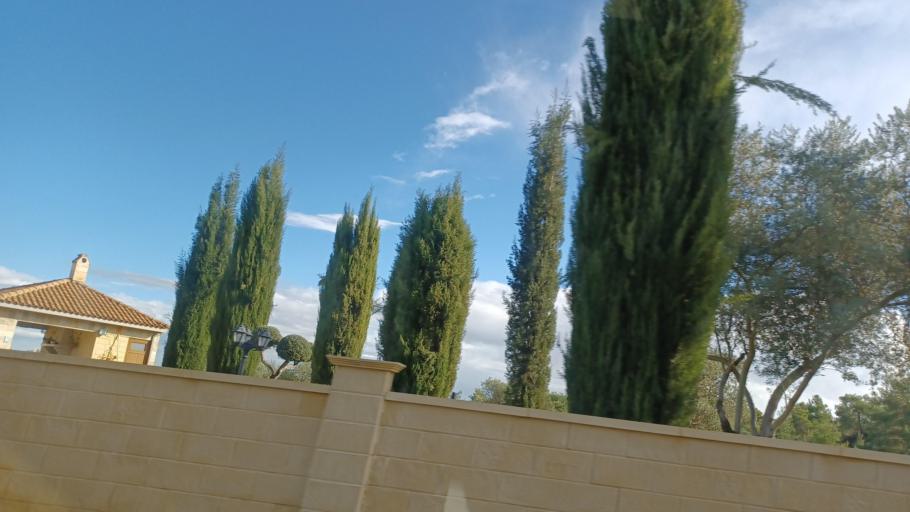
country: CY
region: Lefkosia
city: Lythrodontas
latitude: 34.9384
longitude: 33.2977
